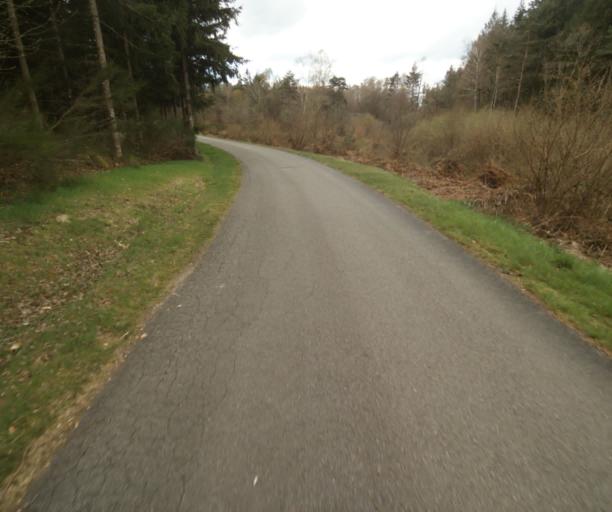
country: FR
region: Limousin
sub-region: Departement de la Correze
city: Correze
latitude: 45.3253
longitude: 1.9405
